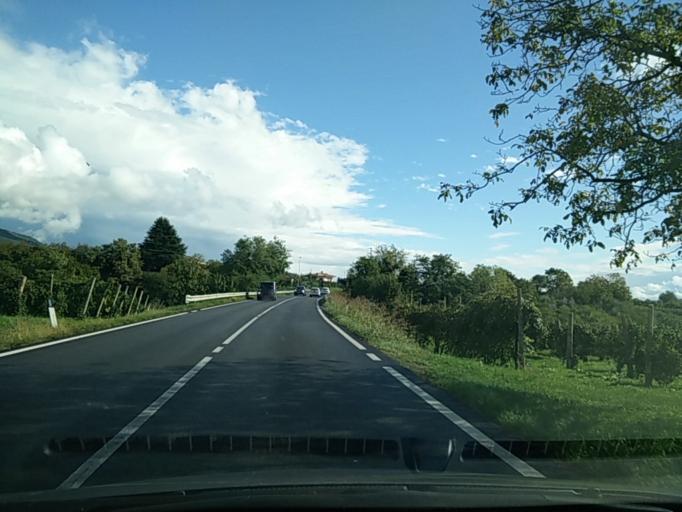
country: IT
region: Veneto
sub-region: Provincia di Treviso
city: Valdobbiadene
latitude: 45.8907
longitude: 11.9798
